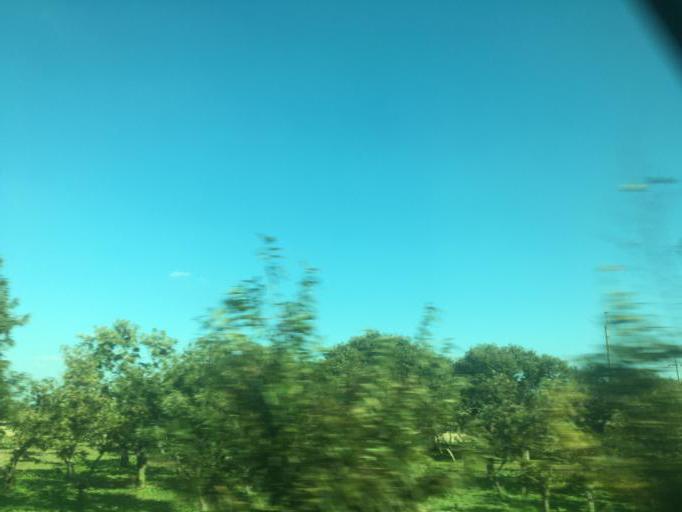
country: JP
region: Ibaraki
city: Tomobe
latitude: 36.2727
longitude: 140.2807
